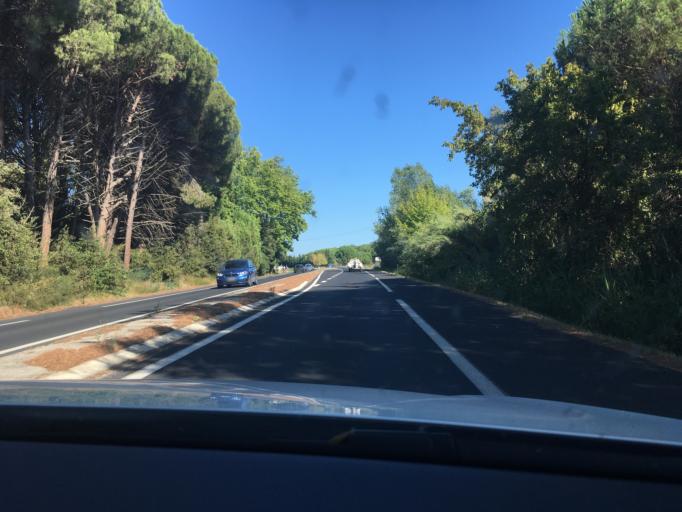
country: FR
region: Languedoc-Roussillon
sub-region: Departement du Gard
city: Aigues-Mortes
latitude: 43.5843
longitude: 4.2327
